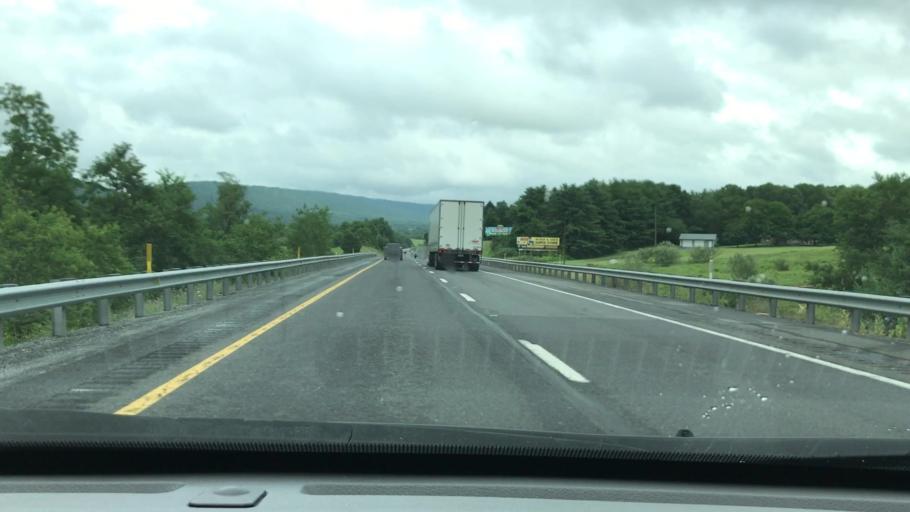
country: US
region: Pennsylvania
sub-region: Bedford County
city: Earlston
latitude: 39.9216
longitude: -78.2344
